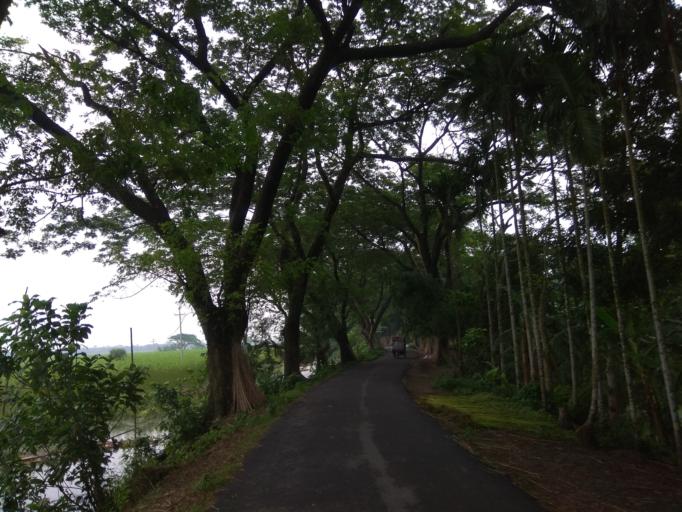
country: BD
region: Dhaka
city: Dohar
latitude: 23.4755
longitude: 90.0569
